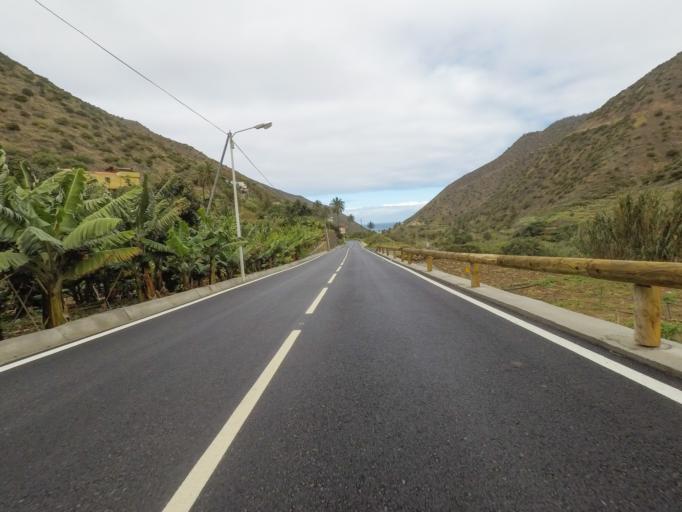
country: ES
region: Canary Islands
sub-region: Provincia de Santa Cruz de Tenerife
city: Vallehermosa
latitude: 28.1852
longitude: -17.2645
